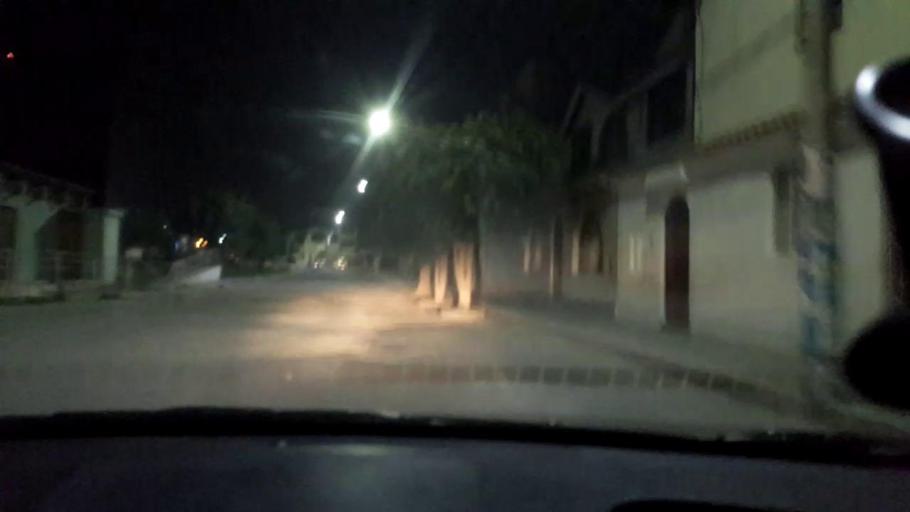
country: PE
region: Lambayeque
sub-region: Provincia de Chiclayo
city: Chiclayo
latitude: -6.7869
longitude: -79.8419
